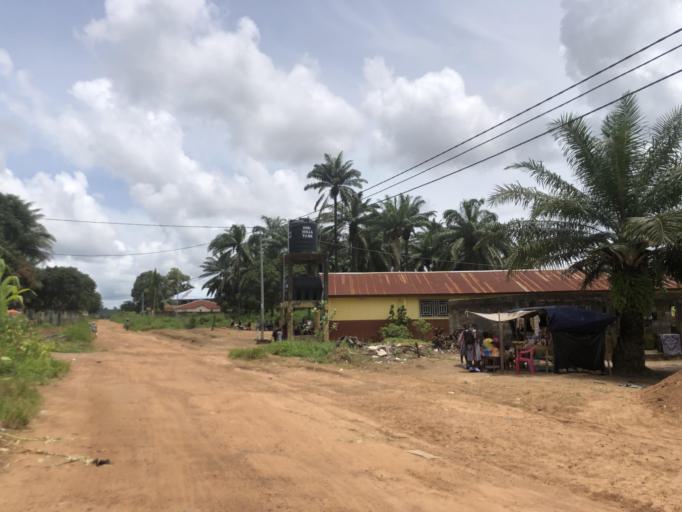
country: SL
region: Northern Province
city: Makeni
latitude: 8.8557
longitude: -12.0551
